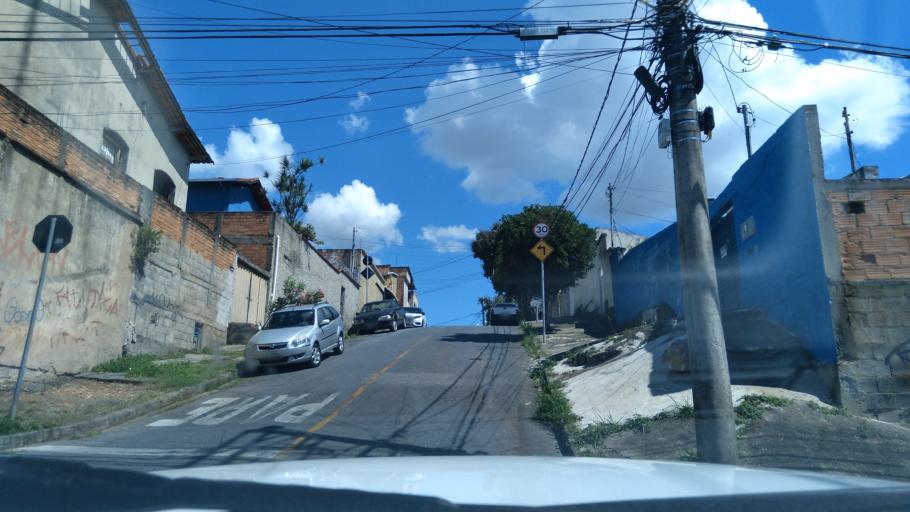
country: BR
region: Minas Gerais
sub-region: Belo Horizonte
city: Belo Horizonte
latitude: -19.8761
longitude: -43.9126
